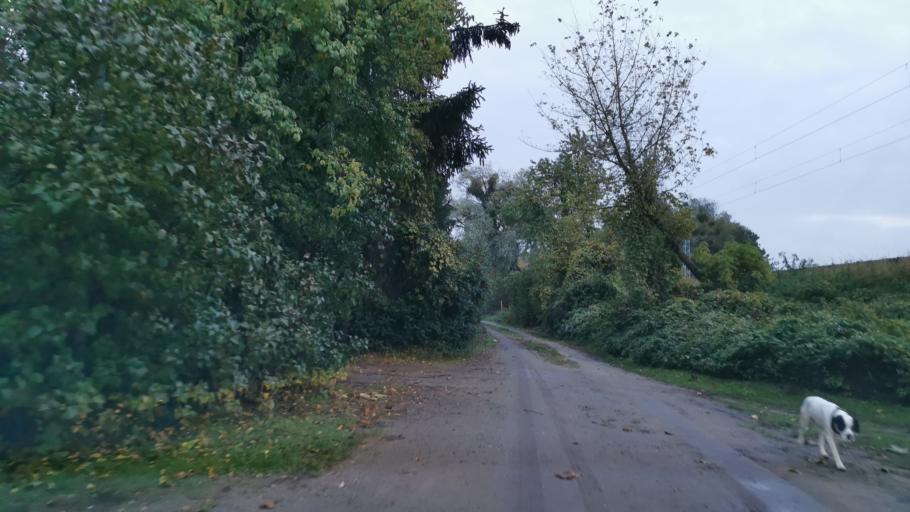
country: DE
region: Brandenburg
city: Michendorf
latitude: 52.3237
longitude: 13.0703
